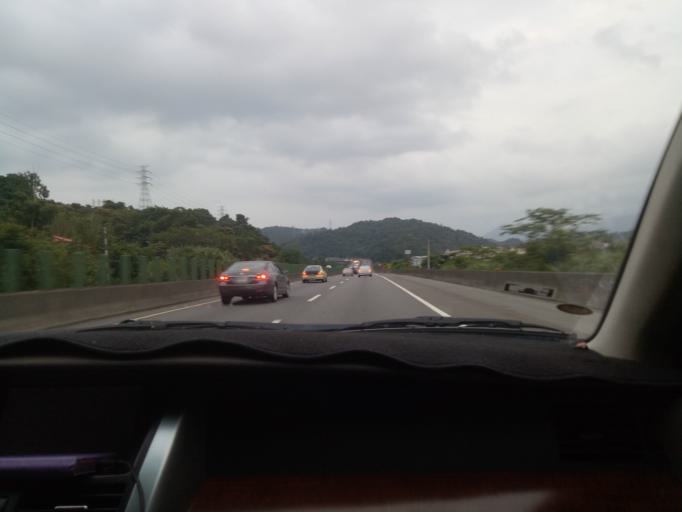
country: TW
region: Taiwan
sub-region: Keelung
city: Keelung
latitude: 25.1020
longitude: 121.7538
